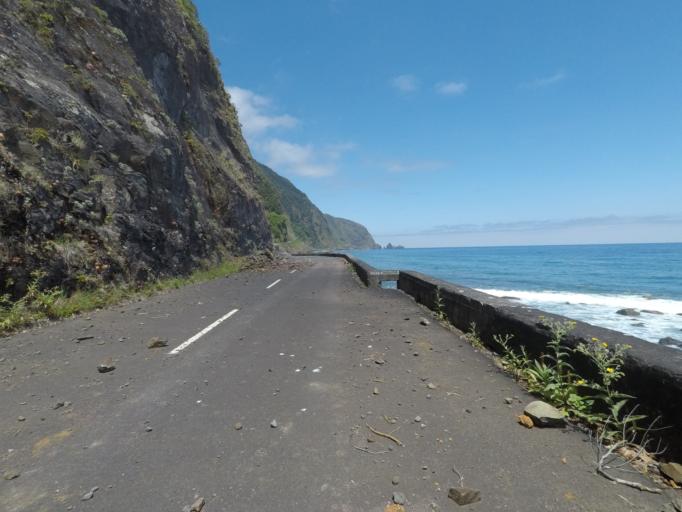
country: PT
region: Madeira
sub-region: Porto Moniz
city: Porto Moniz
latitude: 32.8269
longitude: -17.1237
